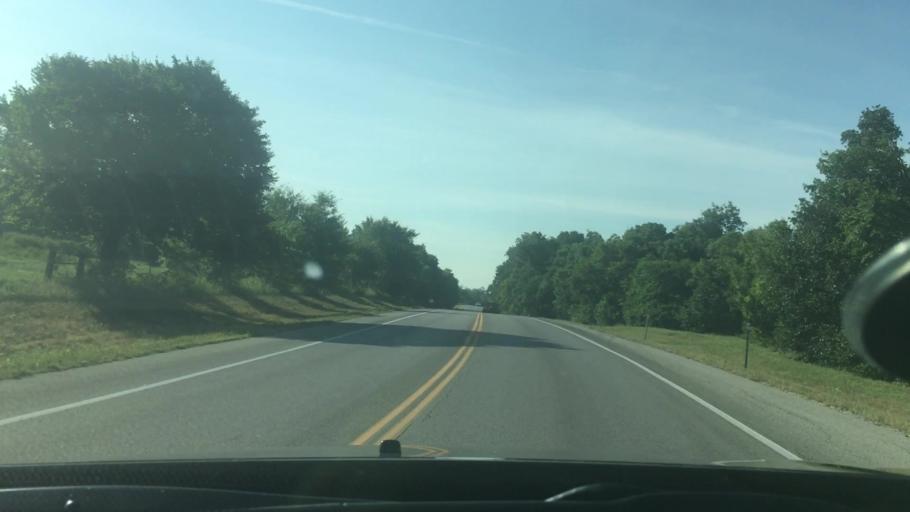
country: US
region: Oklahoma
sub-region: Garvin County
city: Pauls Valley
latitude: 34.6841
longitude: -97.2123
